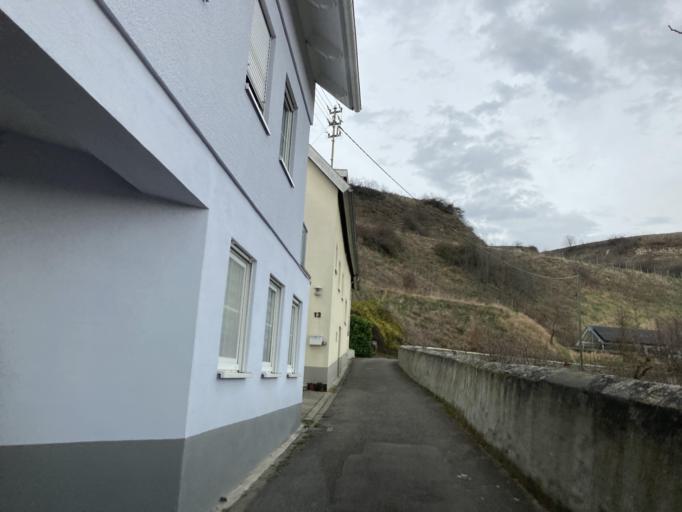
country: DE
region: Baden-Wuerttemberg
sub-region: Freiburg Region
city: Vogtsburg
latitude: 48.0908
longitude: 7.6330
